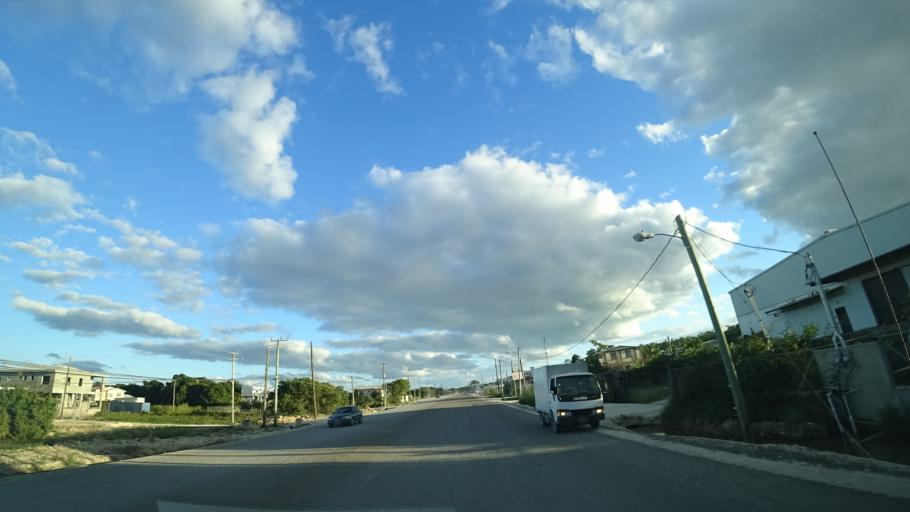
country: BZ
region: Belize
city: Belize City
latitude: 17.5264
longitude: -88.2374
